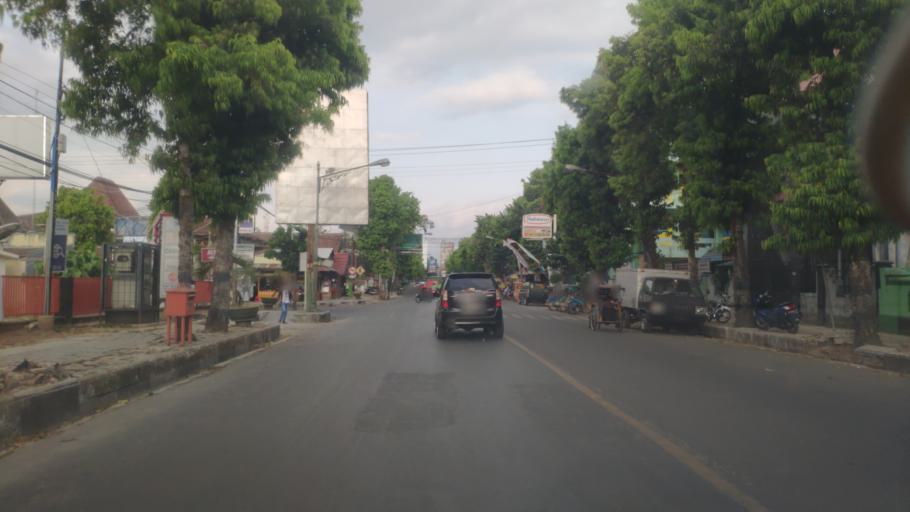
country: ID
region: Central Java
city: Wonosobo
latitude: -7.3967
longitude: 109.6984
